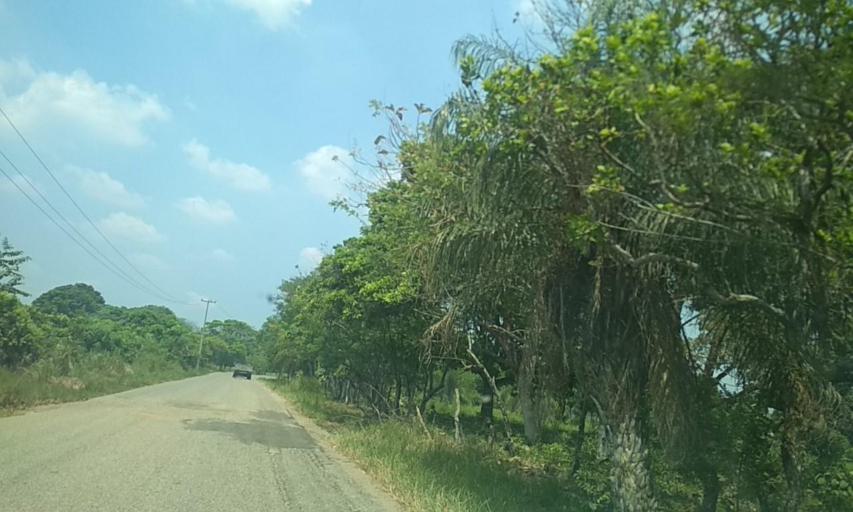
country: MX
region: Tabasco
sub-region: Huimanguillo
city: C-41 (Licenciado Carlos A. Madrazo)
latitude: 17.8299
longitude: -93.5099
